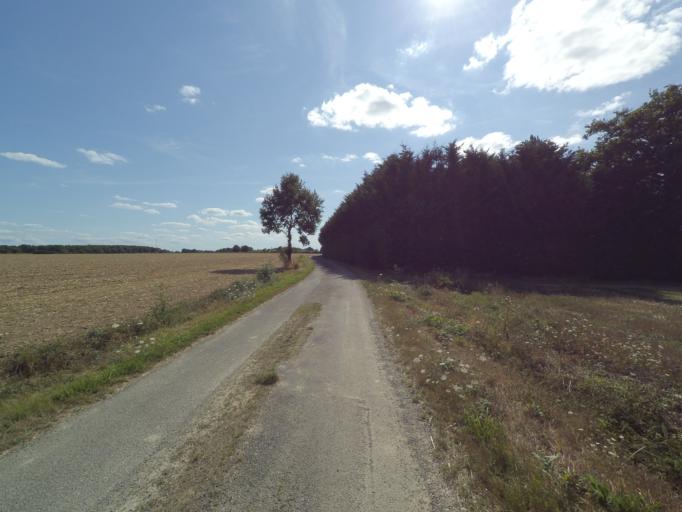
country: FR
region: Pays de la Loire
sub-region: Departement de la Loire-Atlantique
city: Vieillevigne
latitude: 46.9586
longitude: -1.4503
